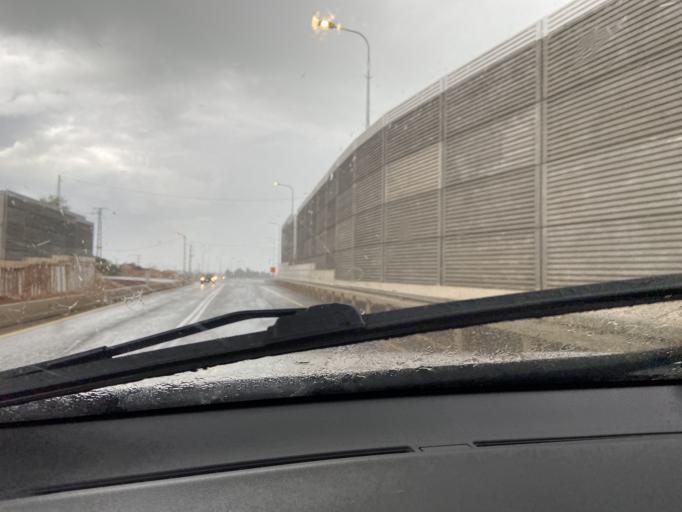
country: IL
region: Northern District
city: El Mazra`a
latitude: 32.9807
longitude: 35.0983
